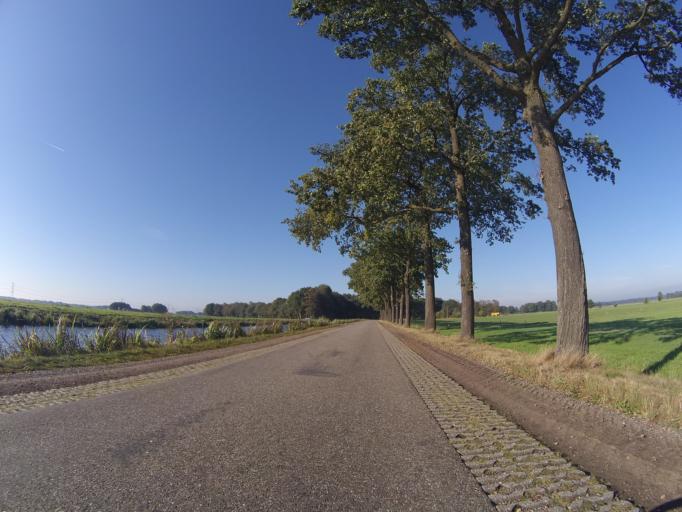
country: NL
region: Drenthe
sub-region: Gemeente Coevorden
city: Sleen
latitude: 52.7388
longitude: 6.7764
